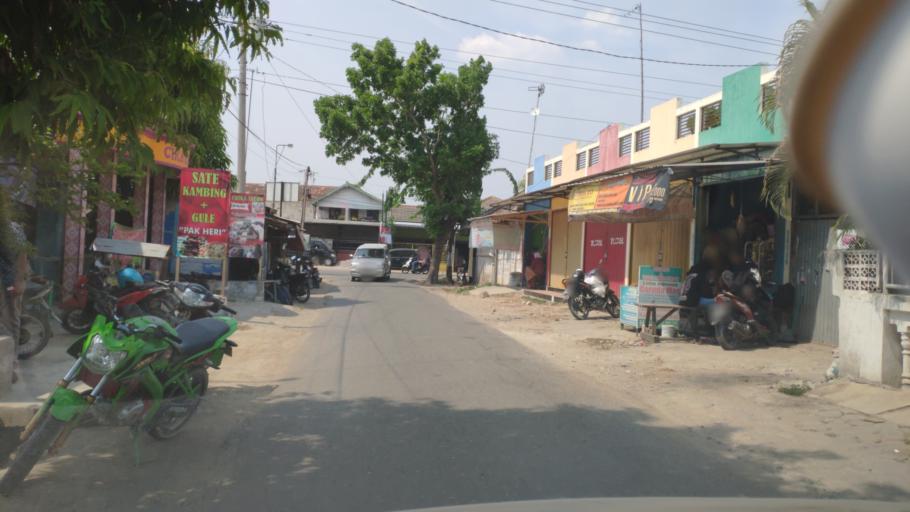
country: ID
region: Central Java
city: Jagong
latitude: -7.0515
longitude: 111.2323
